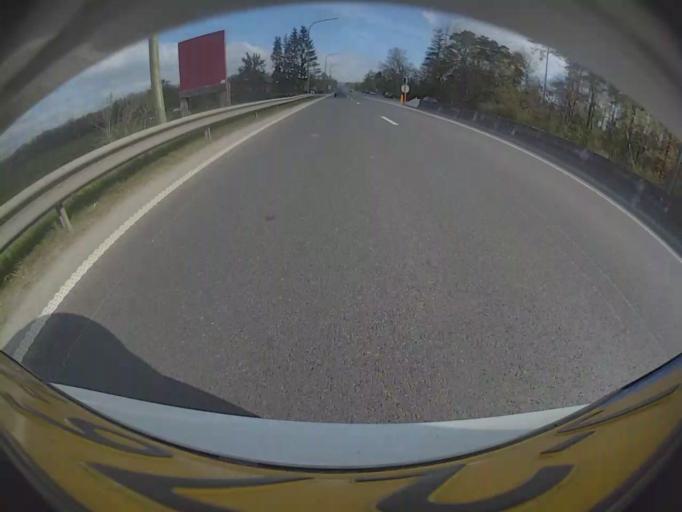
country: BE
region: Wallonia
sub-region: Province du Luxembourg
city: Marche-en-Famenne
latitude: 50.2641
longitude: 5.3468
